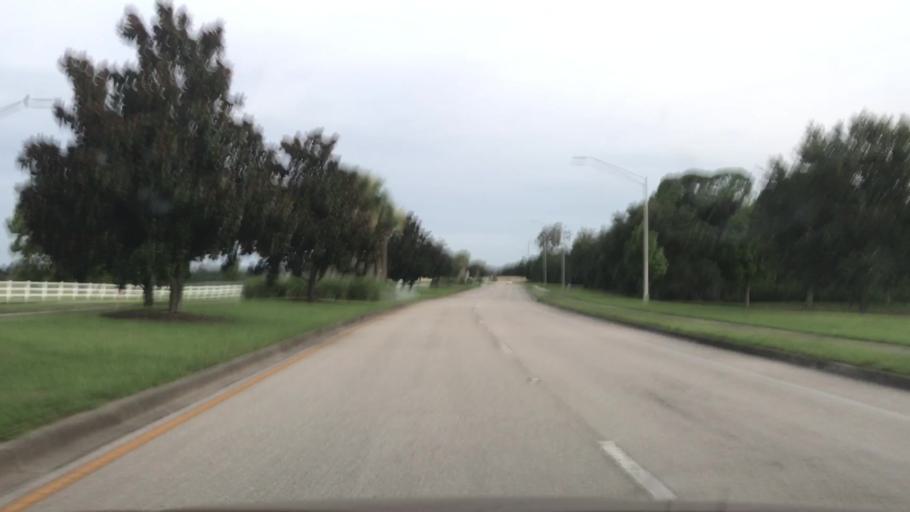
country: US
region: Florida
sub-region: Sarasota County
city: The Meadows
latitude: 27.4374
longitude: -82.4121
